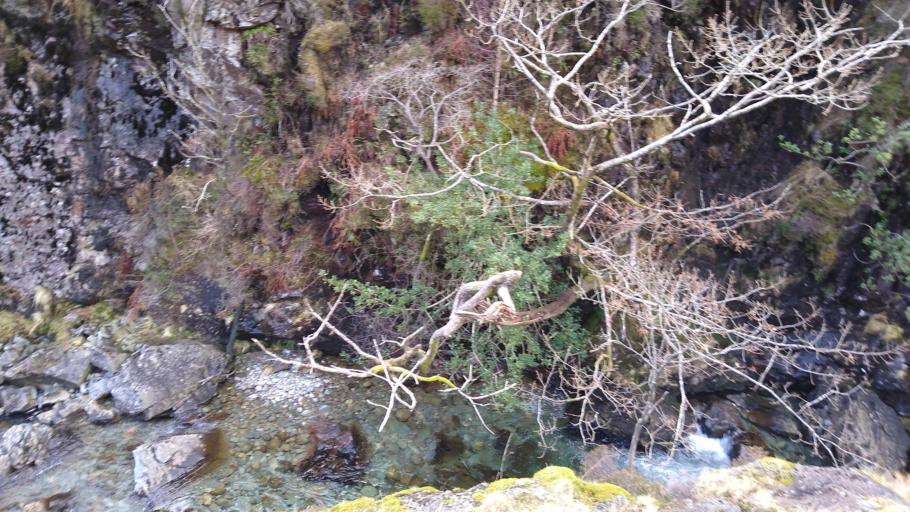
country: GB
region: England
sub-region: Cumbria
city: Keswick
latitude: 54.4248
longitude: -3.1911
